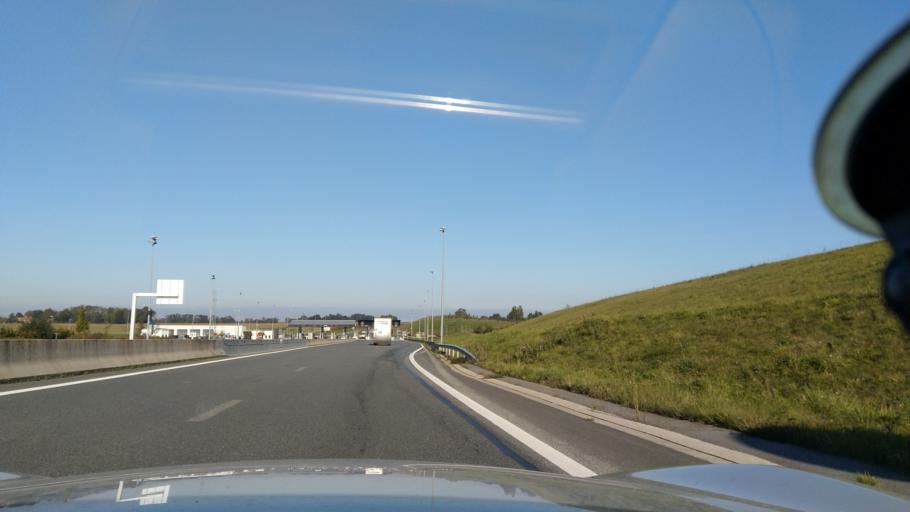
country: FR
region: Haute-Normandie
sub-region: Departement de la Seine-Maritime
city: Villers-Ecalles
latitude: 49.5458
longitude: 0.9246
